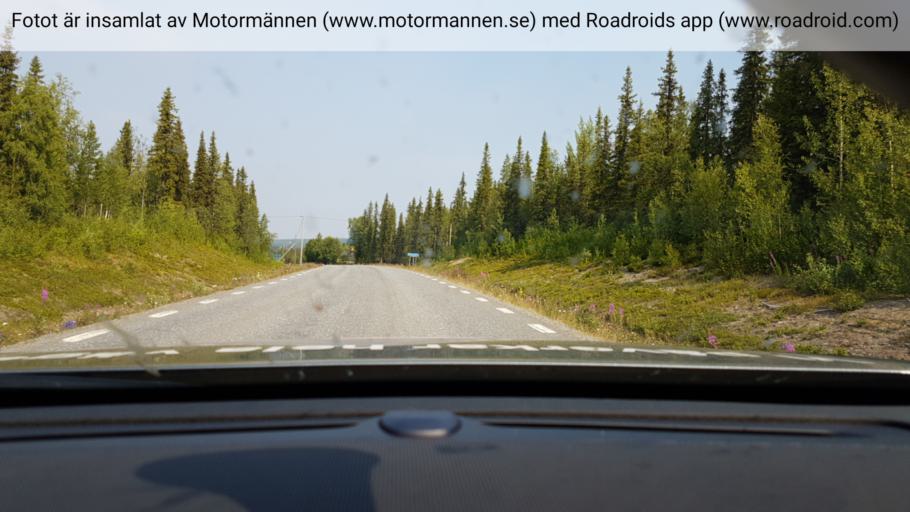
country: SE
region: Vaesterbotten
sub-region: Vilhelmina Kommun
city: Sjoberg
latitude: 65.4483
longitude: 16.1019
